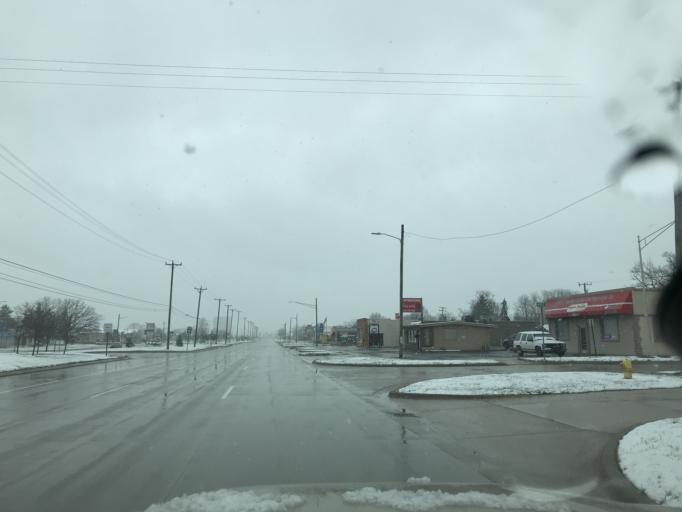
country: US
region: Michigan
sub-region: Wayne County
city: Riverview
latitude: 42.1737
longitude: -83.1888
